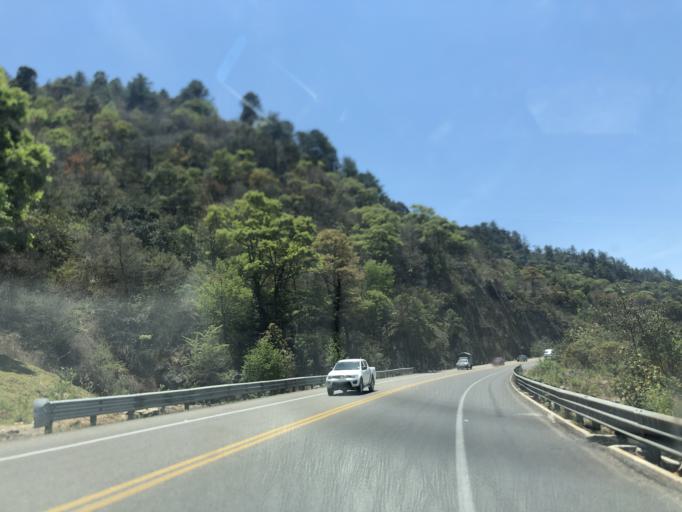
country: MX
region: Chiapas
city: San Cristobal de las Casas
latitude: 16.7187
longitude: -92.6763
